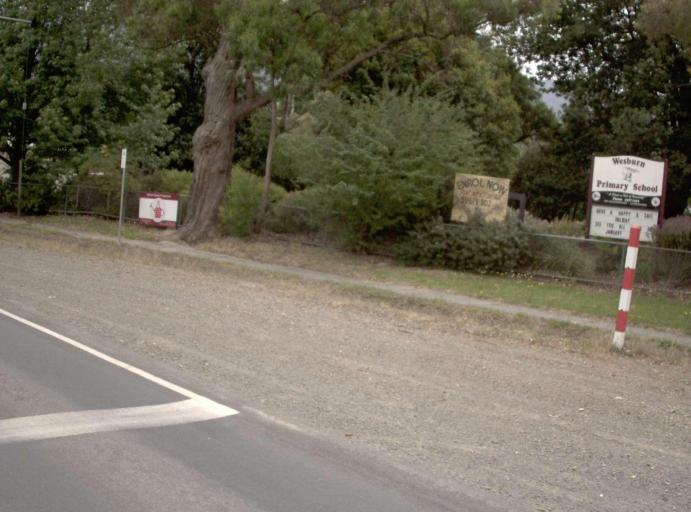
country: AU
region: Victoria
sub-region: Yarra Ranges
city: Millgrove
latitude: -37.7690
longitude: 145.6465
